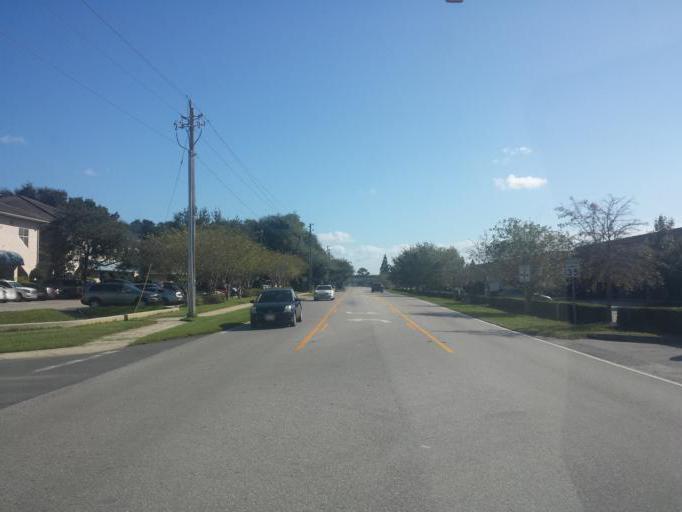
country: US
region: Florida
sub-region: Polk County
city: Crystal Lake
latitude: 28.0168
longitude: -81.9146
